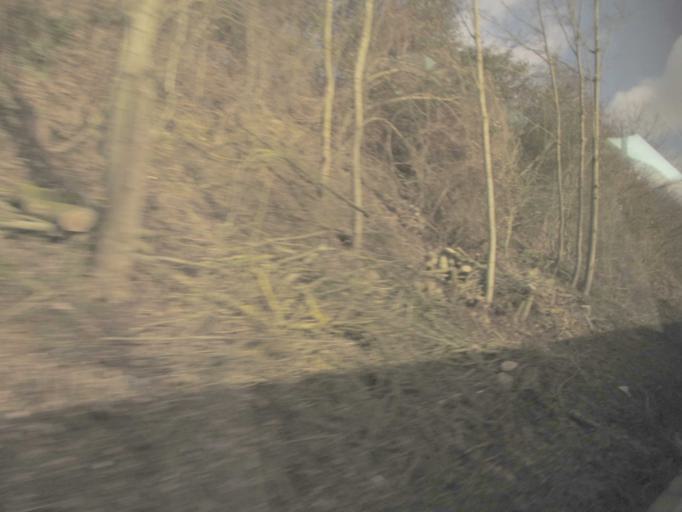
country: GB
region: England
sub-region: Royal Borough of Windsor and Maidenhead
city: White Waltham
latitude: 51.4947
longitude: -0.8040
